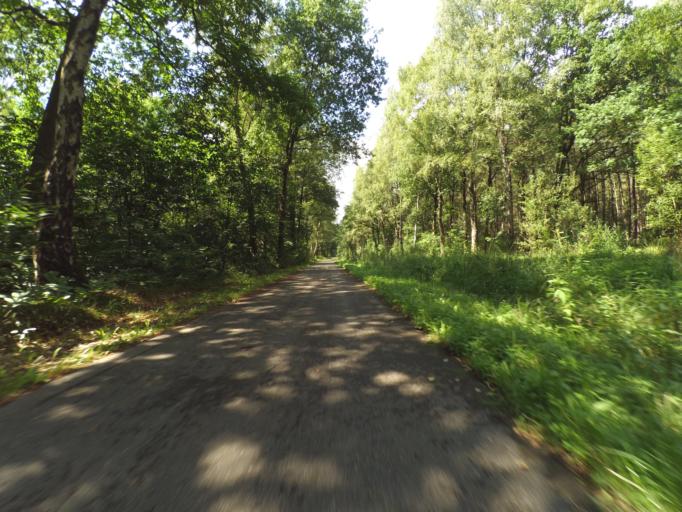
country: BE
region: Flanders
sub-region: Provincie Limburg
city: Bree
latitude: 51.0859
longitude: 5.6429
